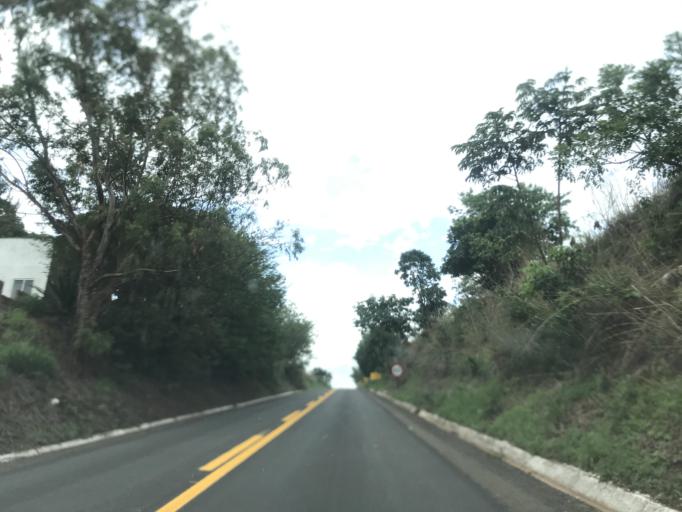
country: BR
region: Goias
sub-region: Bela Vista De Goias
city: Bela Vista de Goias
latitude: -17.0630
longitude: -48.6576
